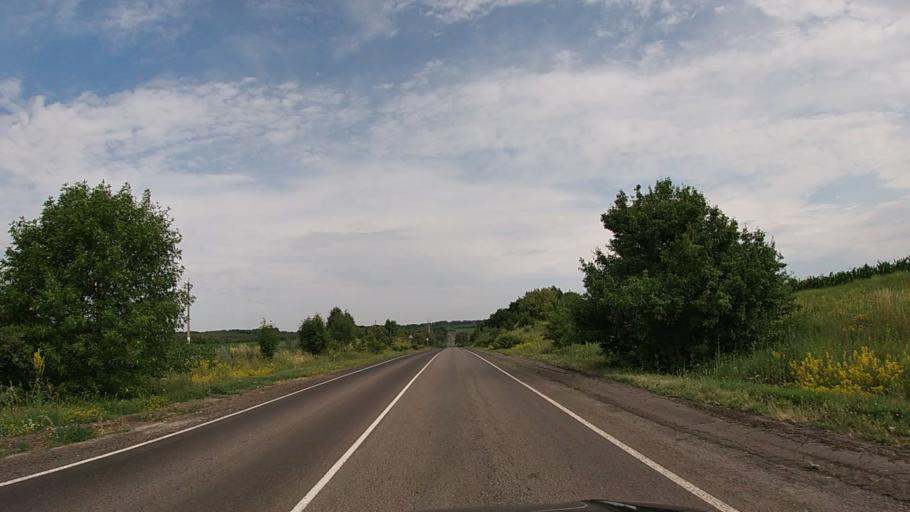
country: RU
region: Belgorod
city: Krasnaya Yaruga
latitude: 50.8227
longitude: 35.5010
